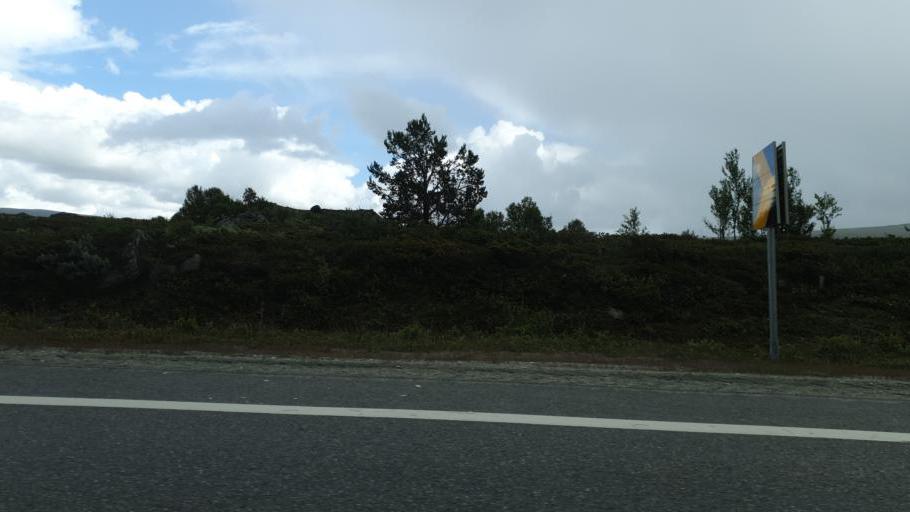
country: NO
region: Sor-Trondelag
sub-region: Oppdal
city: Oppdal
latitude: 62.2681
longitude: 9.5834
